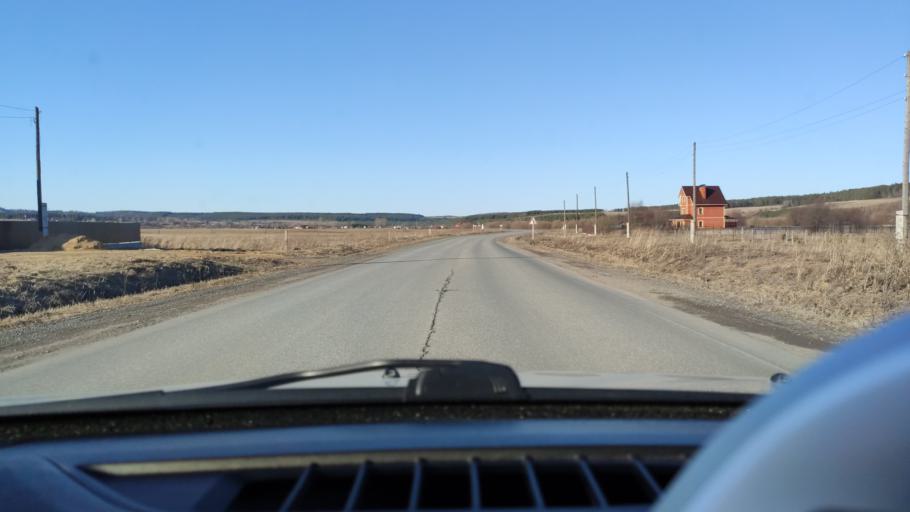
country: RU
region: Perm
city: Suksun
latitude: 57.0404
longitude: 57.4200
